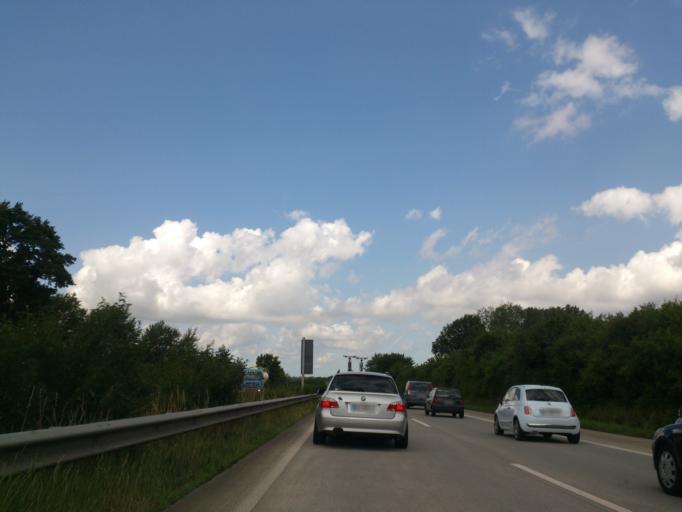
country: DE
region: Schleswig-Holstein
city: Neuenbrook
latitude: 53.8783
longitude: 9.5523
